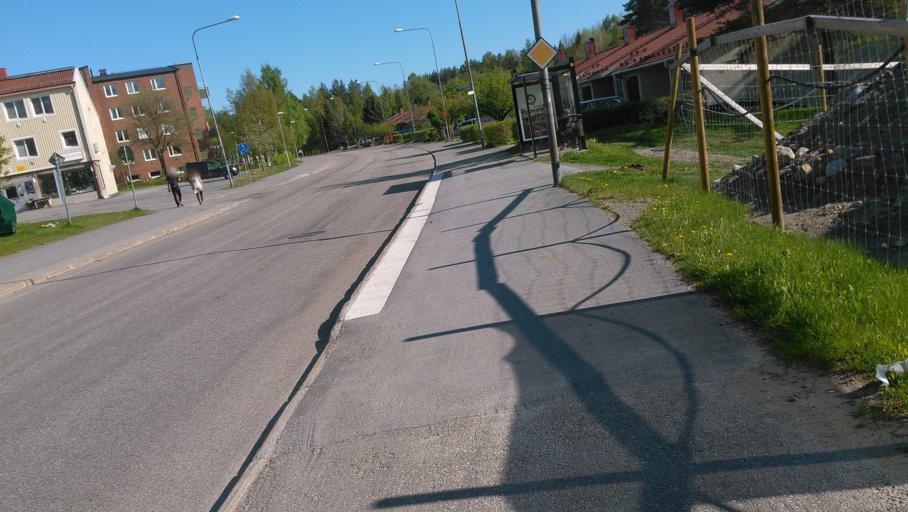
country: SE
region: Vaesterbotten
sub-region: Umea Kommun
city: Umea
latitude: 63.8255
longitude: 20.2946
